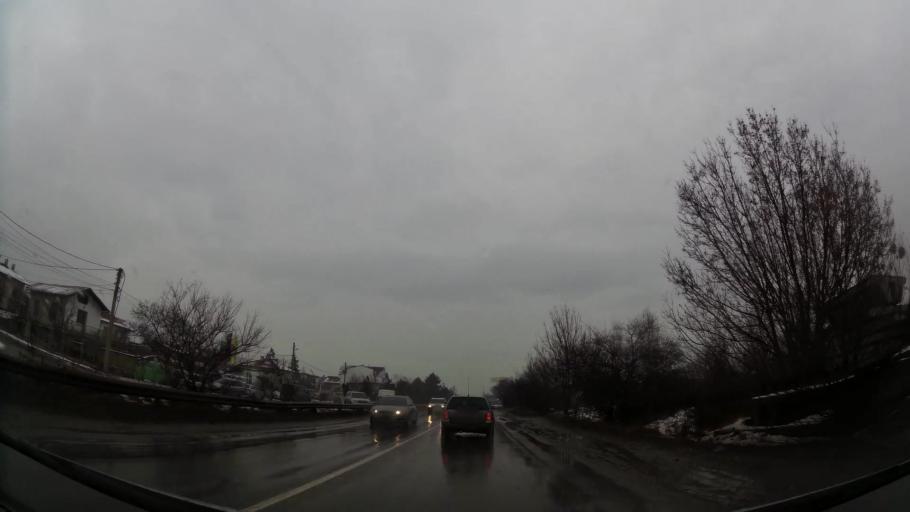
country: BG
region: Sofiya
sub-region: Obshtina Bozhurishte
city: Bozhurishte
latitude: 42.6926
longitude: 23.2303
